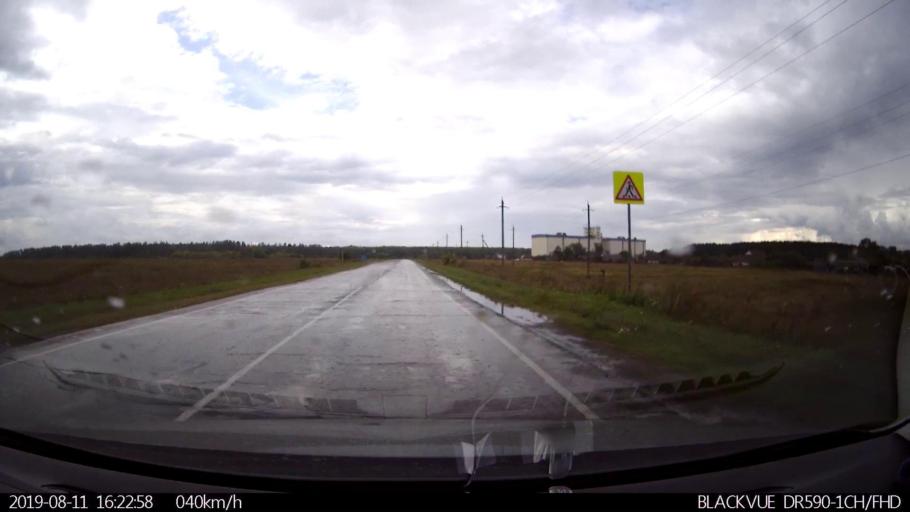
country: RU
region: Ulyanovsk
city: Mayna
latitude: 54.0918
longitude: 47.5905
